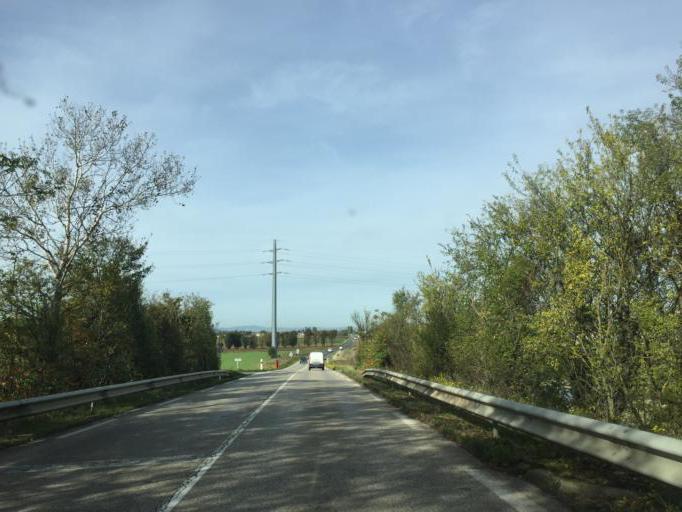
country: FR
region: Rhone-Alpes
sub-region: Departement du Rhone
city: Montanay
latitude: 45.8820
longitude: 4.8964
